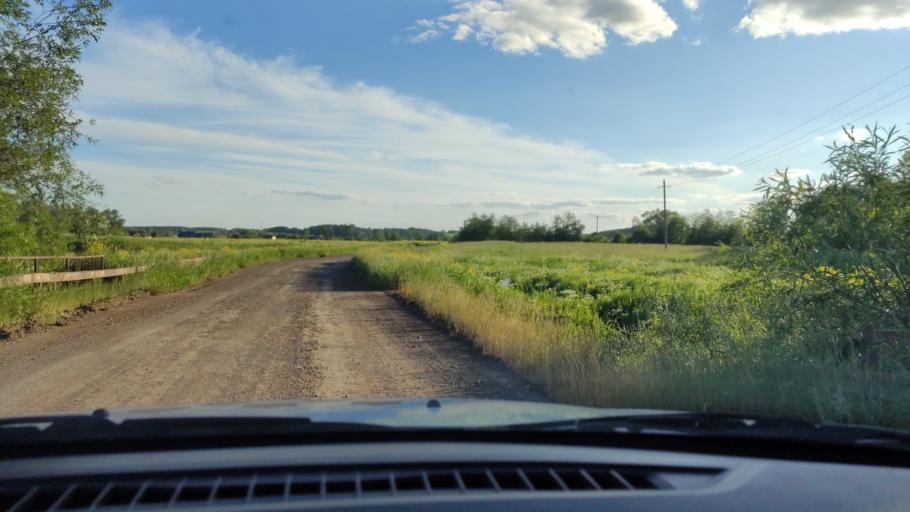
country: RU
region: Perm
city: Orda
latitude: 57.3014
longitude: 56.6289
